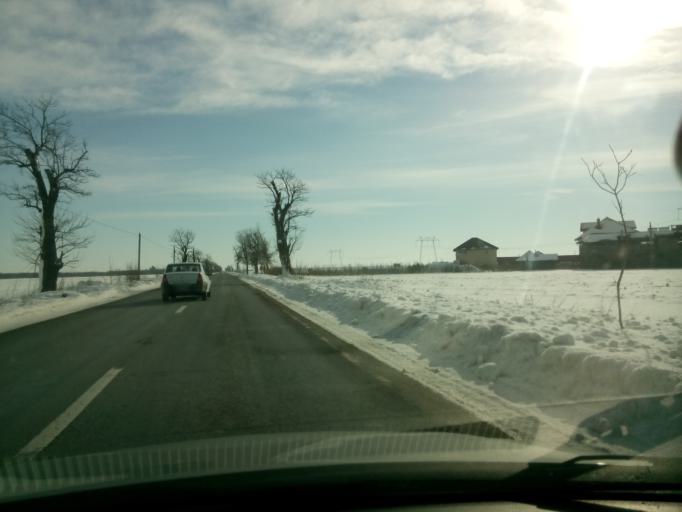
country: RO
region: Calarasi
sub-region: Comuna Frumusani
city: Frumusani
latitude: 44.2637
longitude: 26.3532
